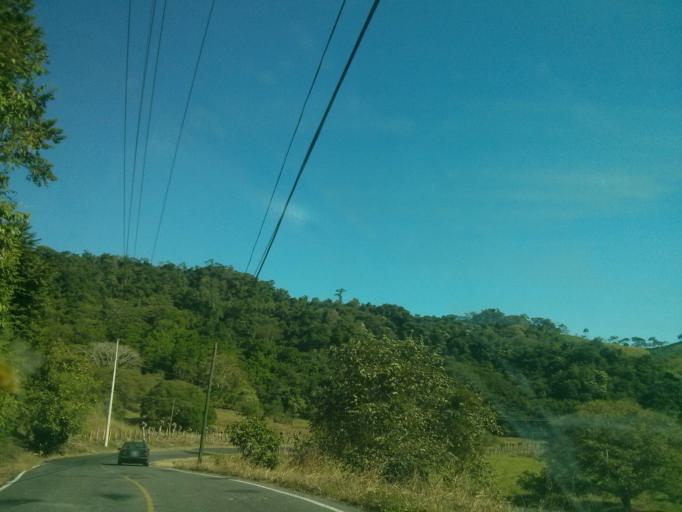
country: CR
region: Puntarenas
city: Paquera
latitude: 9.7666
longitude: -84.9825
